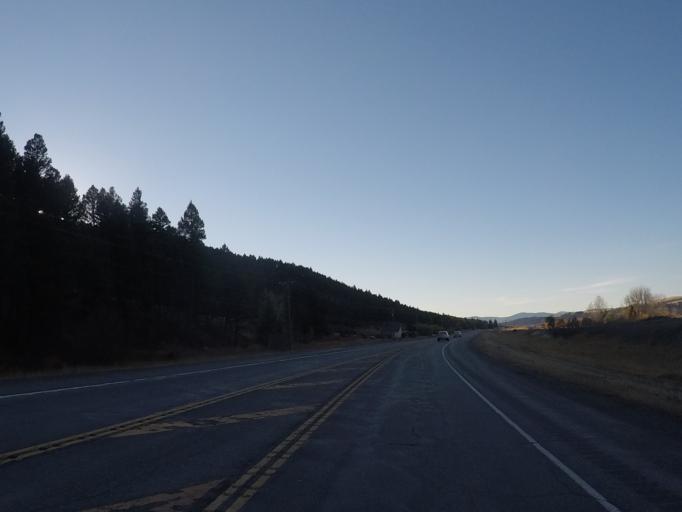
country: US
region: Montana
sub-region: Lewis and Clark County
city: Helena West Side
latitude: 46.5568
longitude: -112.4147
